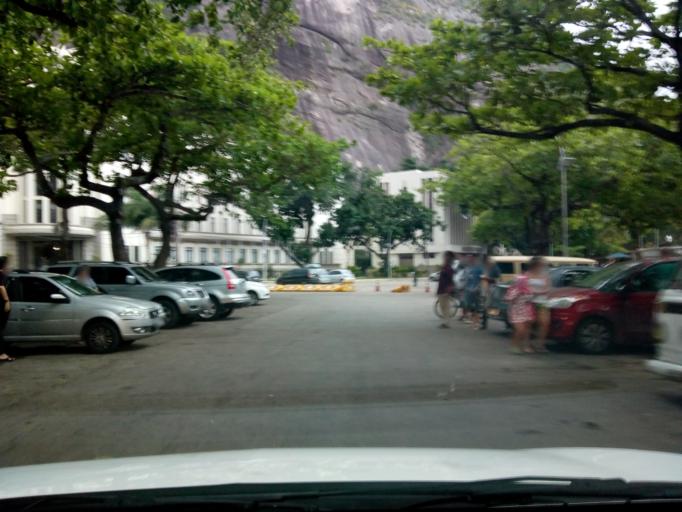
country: BR
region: Rio de Janeiro
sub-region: Rio De Janeiro
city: Rio de Janeiro
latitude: -22.9550
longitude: -43.1654
